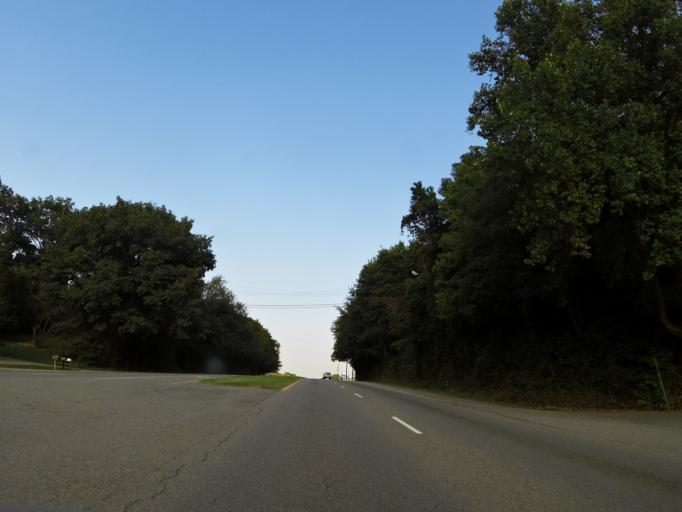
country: US
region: Tennessee
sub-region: Knox County
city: Mascot
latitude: 36.0179
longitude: -83.8139
